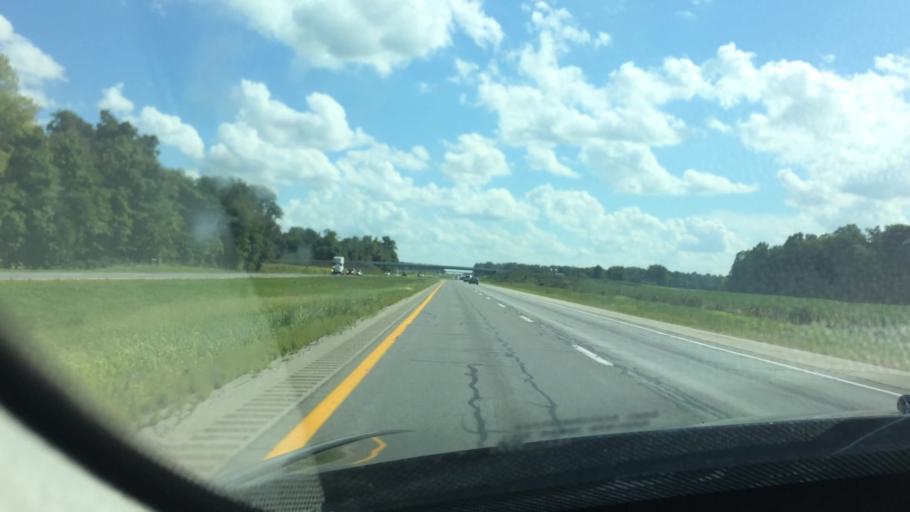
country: US
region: Ohio
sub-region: Shelby County
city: Botkins
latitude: 40.5158
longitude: -84.1695
